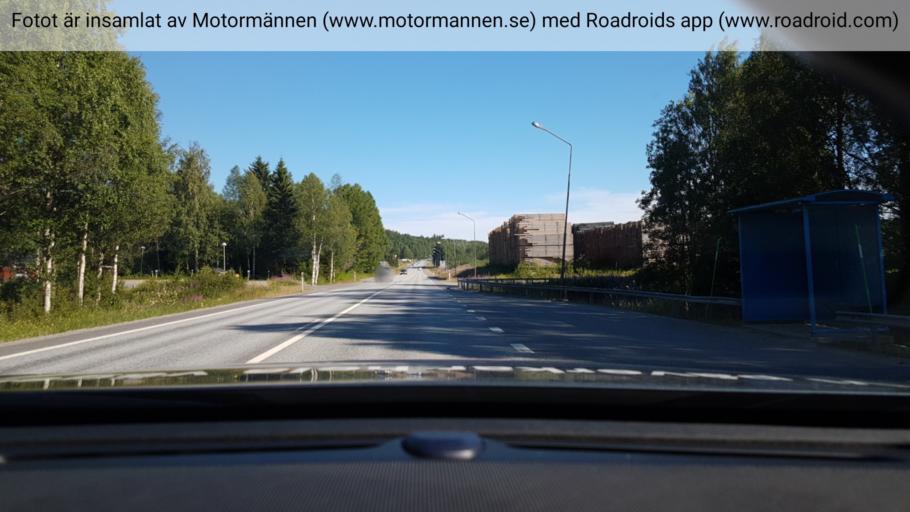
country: SE
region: Vaesterbotten
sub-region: Vannas Kommun
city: Vannasby
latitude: 63.9180
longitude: 19.8745
